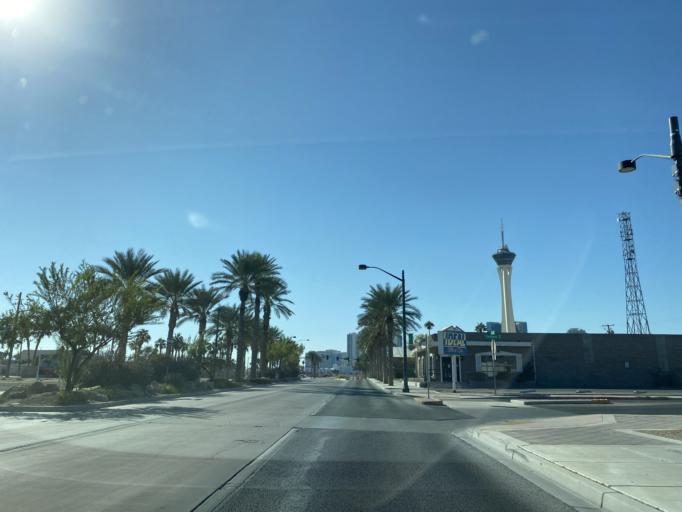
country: US
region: Nevada
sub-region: Clark County
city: Las Vegas
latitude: 36.1576
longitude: -115.1511
